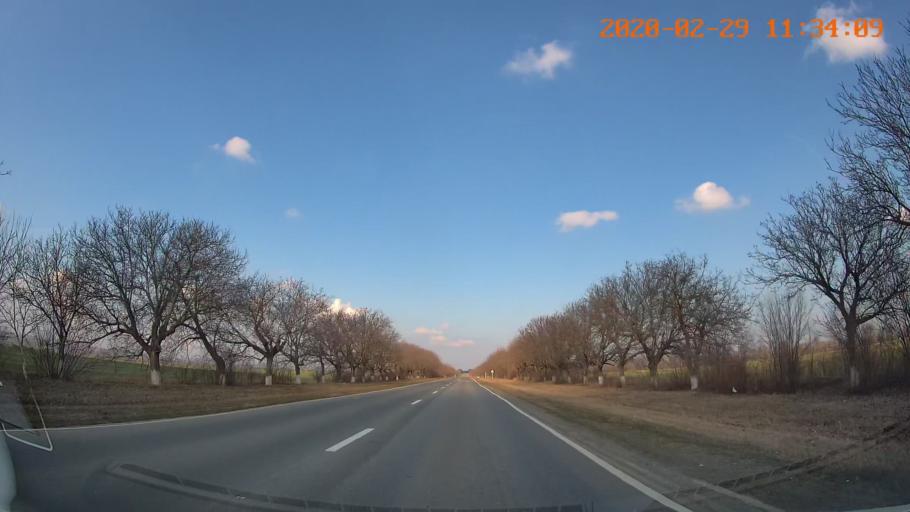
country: MD
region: Rezina
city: Saharna
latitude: 47.5616
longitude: 29.0769
